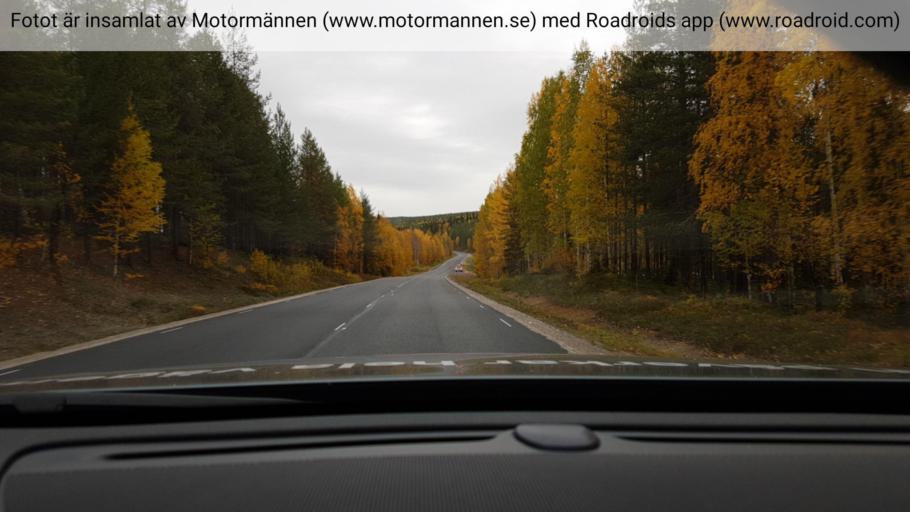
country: SE
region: Norrbotten
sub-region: Overkalix Kommun
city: OEverkalix
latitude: 66.4567
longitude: 22.7899
